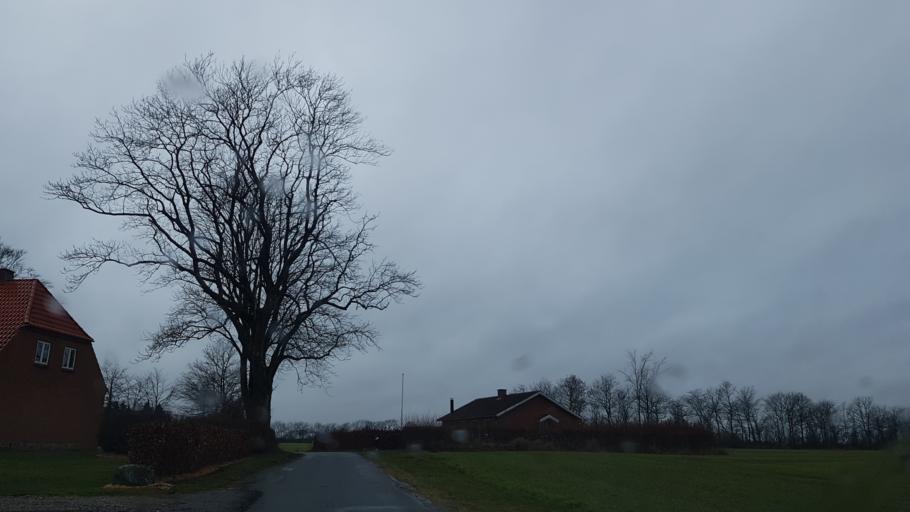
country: DK
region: South Denmark
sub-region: Kolding Kommune
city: Vamdrup
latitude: 55.3848
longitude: 9.2552
